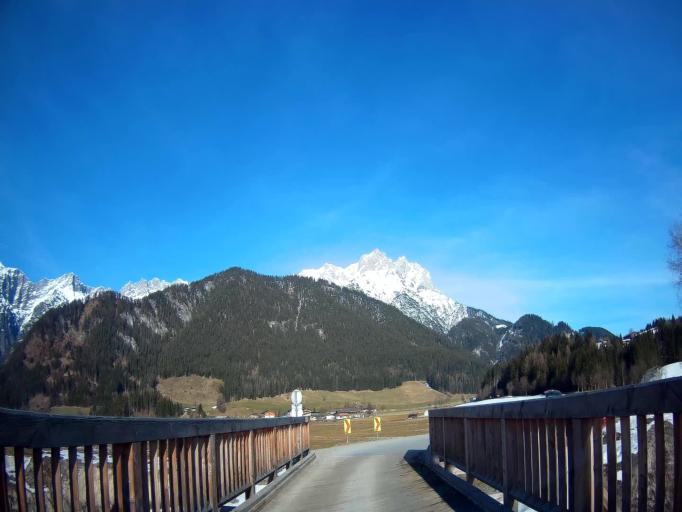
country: AT
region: Salzburg
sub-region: Politischer Bezirk Zell am See
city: Saalfelden am Steinernen Meer
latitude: 47.4525
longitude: 12.8238
